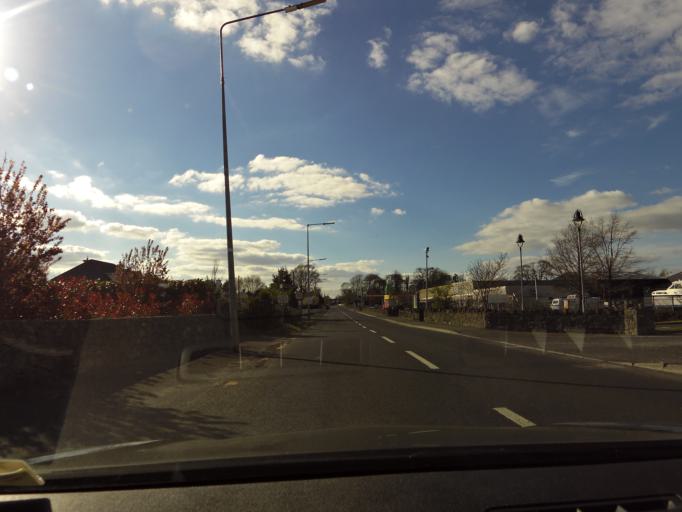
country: IE
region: Connaught
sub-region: County Galway
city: Portumna
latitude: 53.0938
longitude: -8.2021
